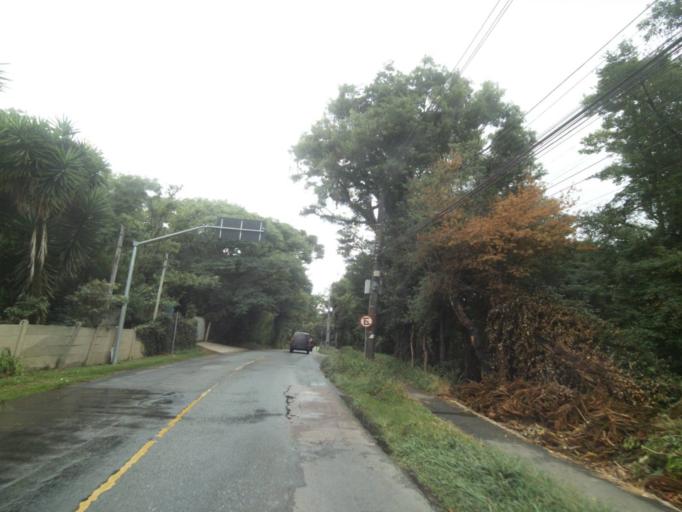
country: BR
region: Parana
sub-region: Curitiba
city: Curitiba
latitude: -25.4421
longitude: -49.3228
